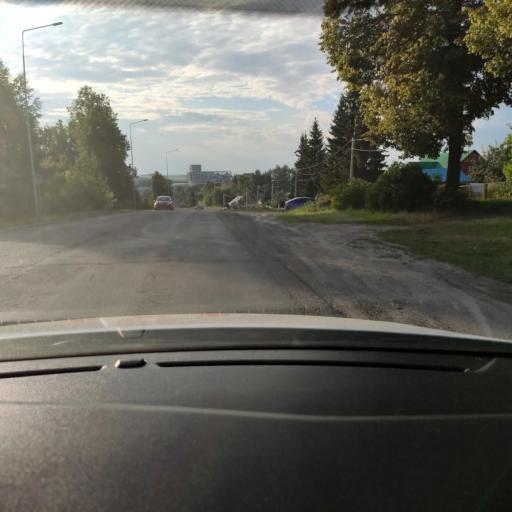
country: RU
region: Tatarstan
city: Vysokaya Gora
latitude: 55.9748
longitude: 49.3108
